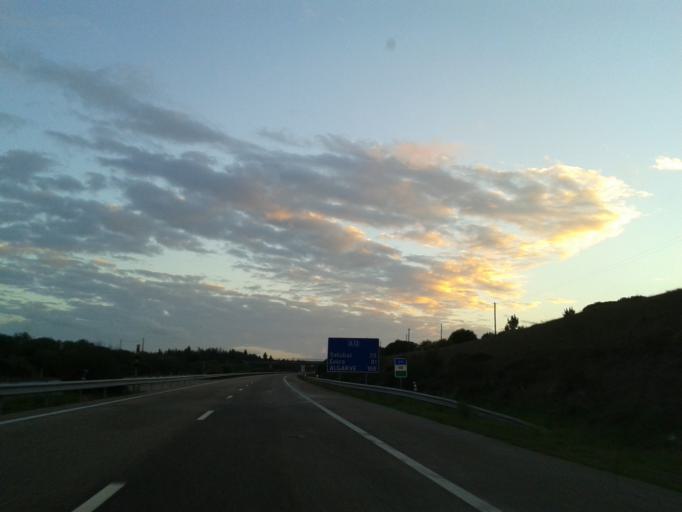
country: PT
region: Evora
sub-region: Vendas Novas
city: Vendas Novas
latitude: 38.6813
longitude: -8.6403
